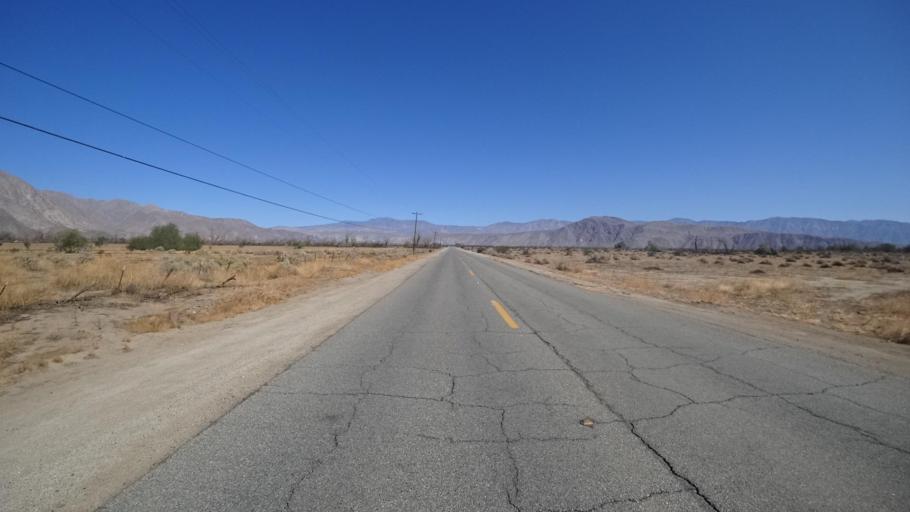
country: US
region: California
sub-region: San Diego County
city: Borrego Springs
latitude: 33.2706
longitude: -116.3662
